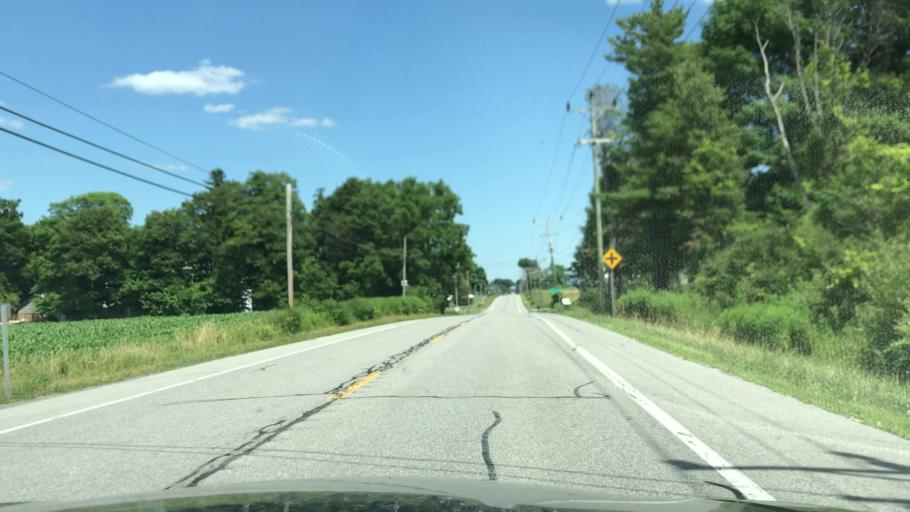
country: US
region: New York
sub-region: Wyoming County
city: Perry
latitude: 42.7447
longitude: -78.0528
